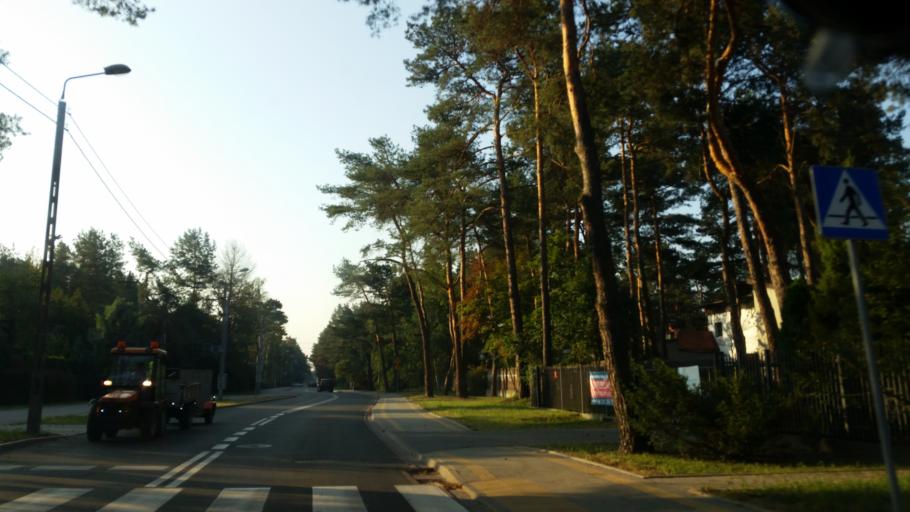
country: PL
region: Masovian Voivodeship
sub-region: Powiat otwocki
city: Jozefow
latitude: 52.1423
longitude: 21.2152
